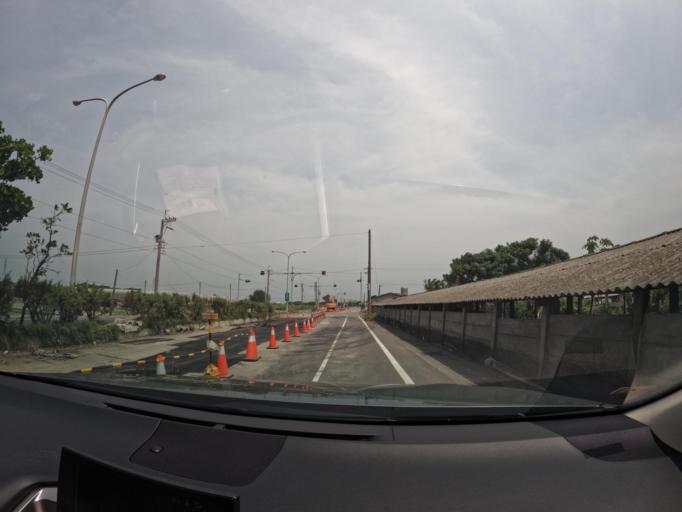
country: TW
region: Taiwan
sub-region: Changhua
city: Chang-hua
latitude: 23.9597
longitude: 120.3650
